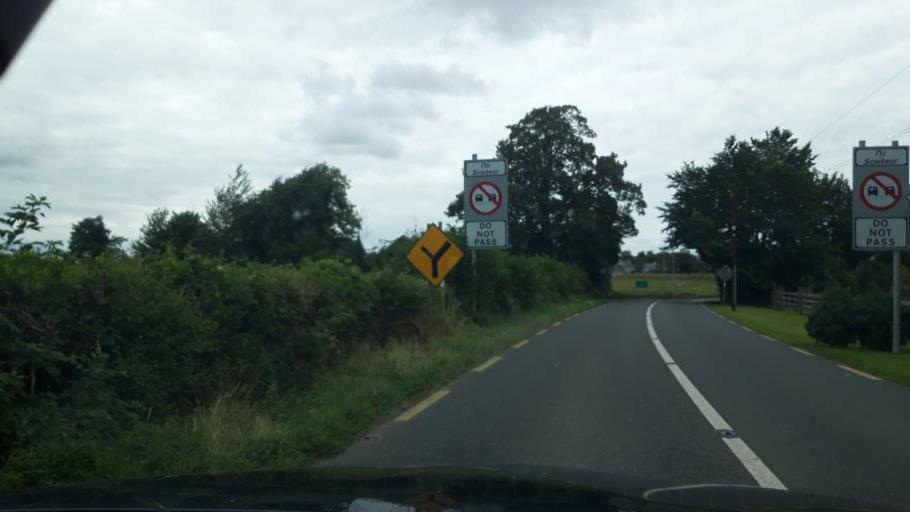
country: IE
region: Leinster
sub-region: Kilkenny
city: Thomastown
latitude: 52.6253
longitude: -7.0720
